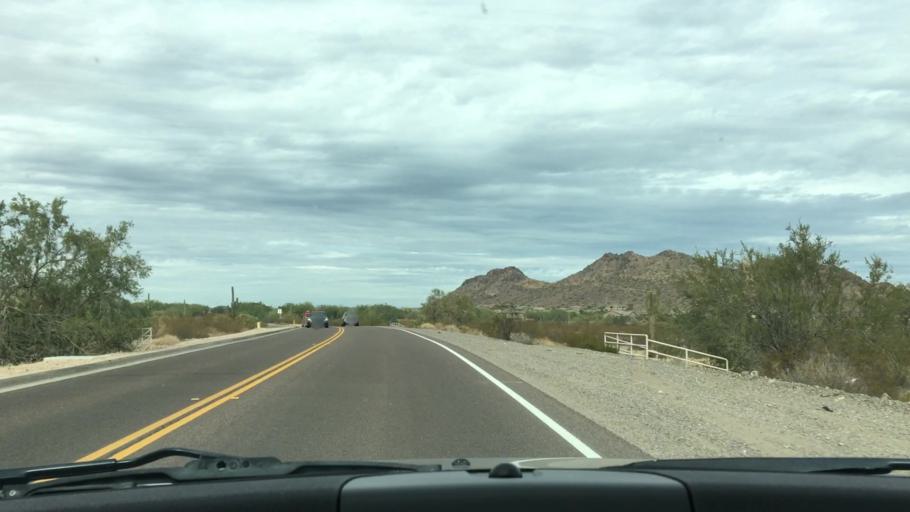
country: US
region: Arizona
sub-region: Maricopa County
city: Sun City West
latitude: 33.7212
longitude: -112.2351
